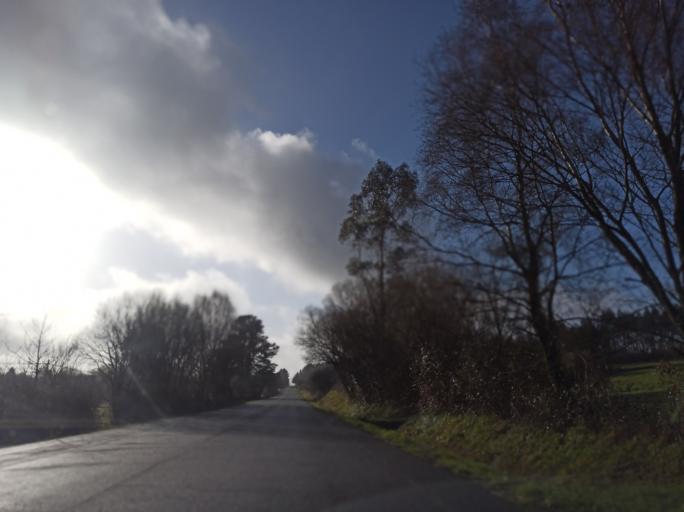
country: ES
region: Galicia
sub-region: Provincia da Coruna
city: Curtis
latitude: 43.0943
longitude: -8.0187
